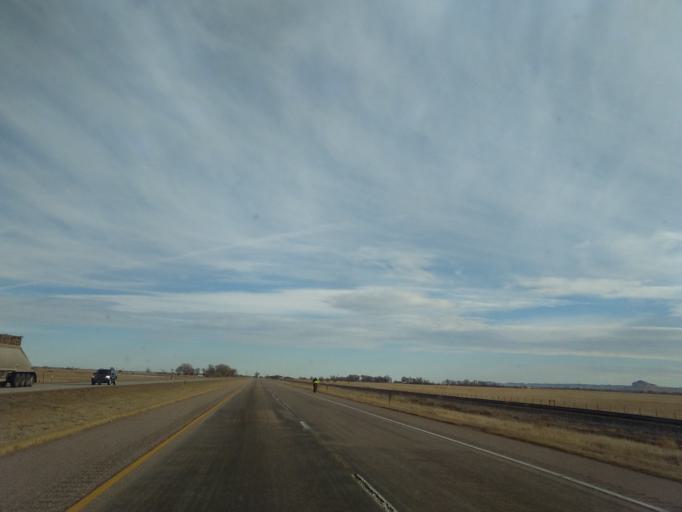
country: US
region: Nebraska
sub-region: Scotts Bluff County
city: Gering
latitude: 41.8241
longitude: -103.5550
